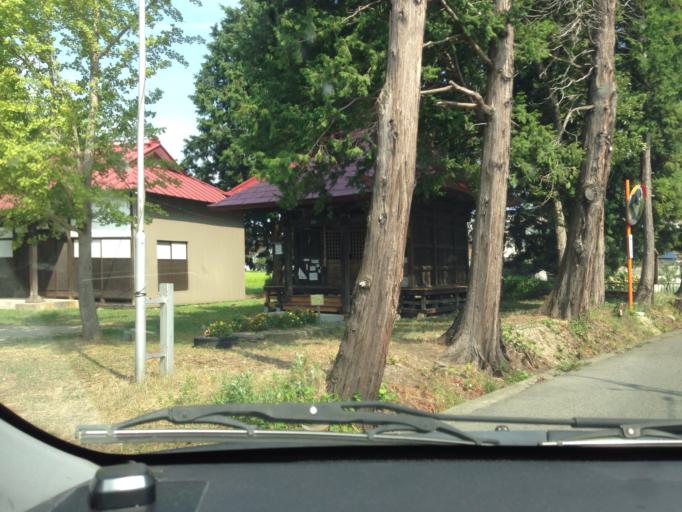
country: JP
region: Fukushima
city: Kitakata
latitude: 37.6369
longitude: 139.8705
